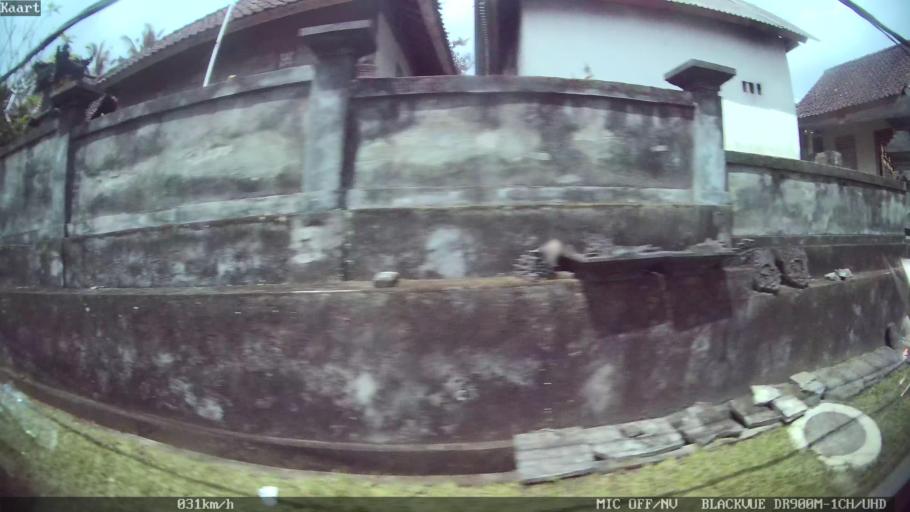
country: ID
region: Bali
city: Banjar Susut Kaja
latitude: -8.4407
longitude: 115.3298
